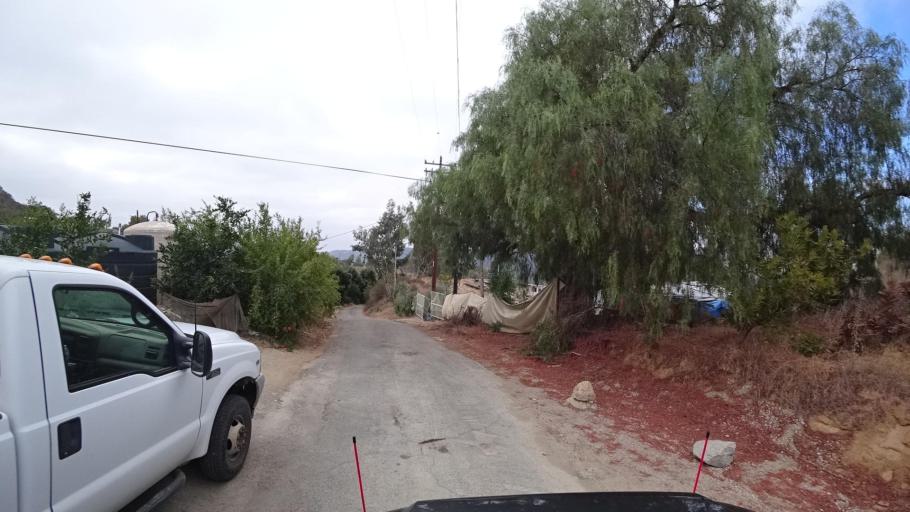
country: US
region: California
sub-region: San Diego County
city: Fallbrook
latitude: 33.4288
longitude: -117.3134
